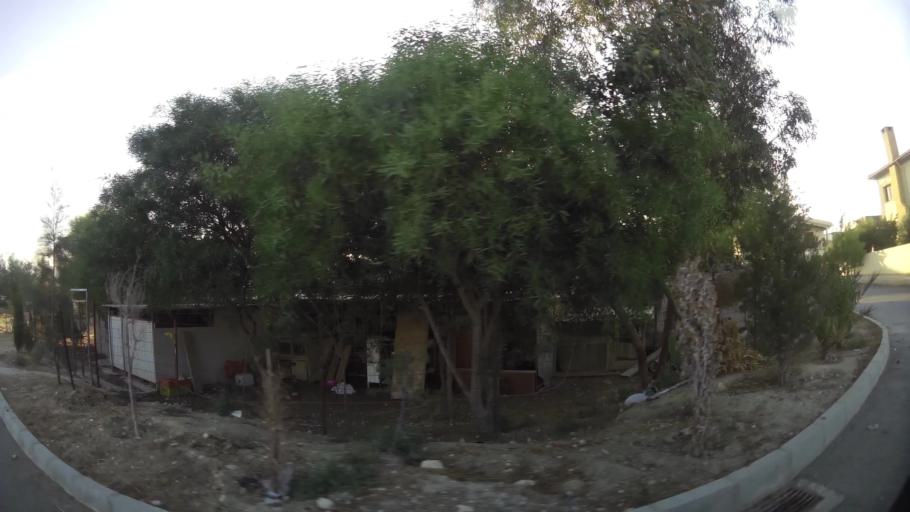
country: CY
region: Lefkosia
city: Nicosia
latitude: 35.1920
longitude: 33.3140
